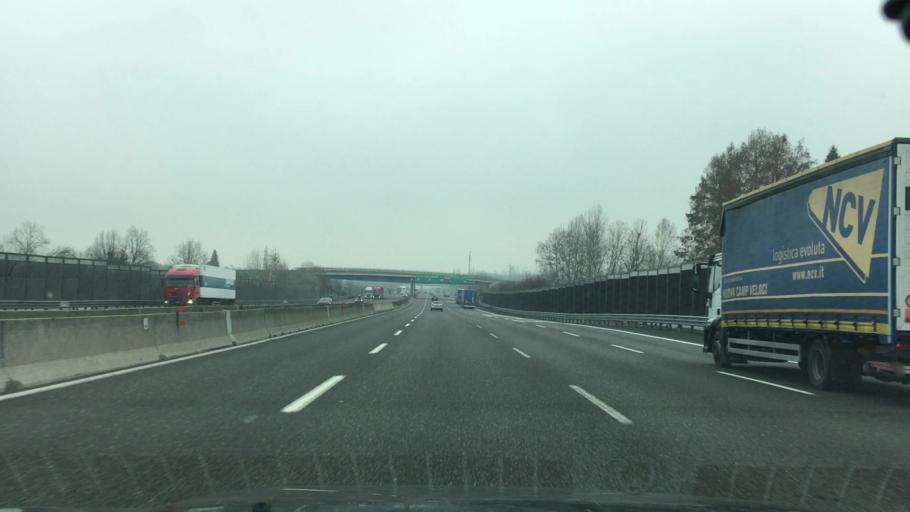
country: IT
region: Emilia-Romagna
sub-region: Provincia di Modena
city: San Damaso
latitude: 44.5806
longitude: 10.9743
